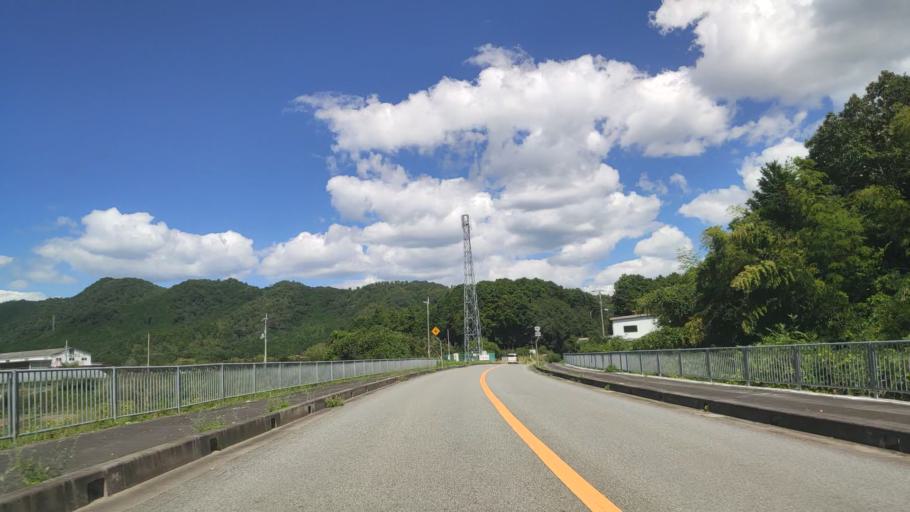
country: JP
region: Kyoto
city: Fukuchiyama
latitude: 35.2417
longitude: 135.1234
